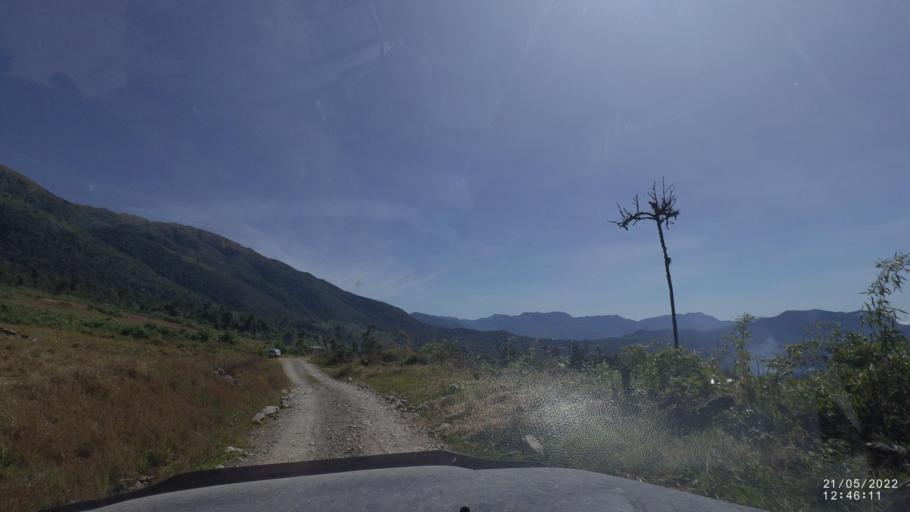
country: BO
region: Cochabamba
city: Colomi
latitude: -17.1853
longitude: -65.9377
